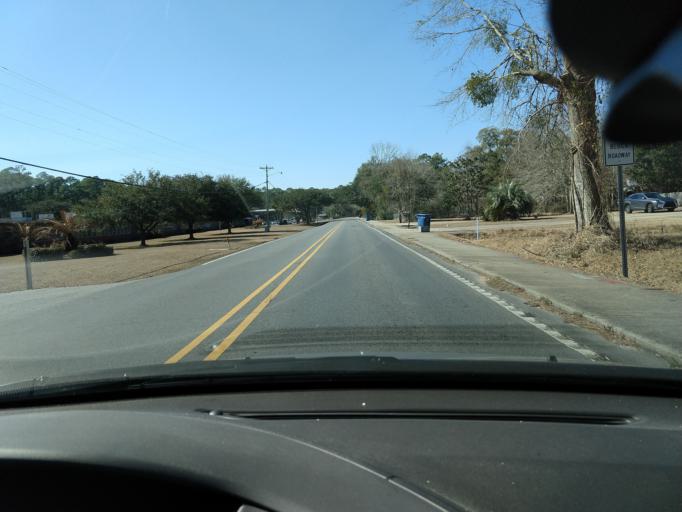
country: US
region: Mississippi
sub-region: Jackson County
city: Gulf Park Estates
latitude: 30.3991
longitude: -88.7786
